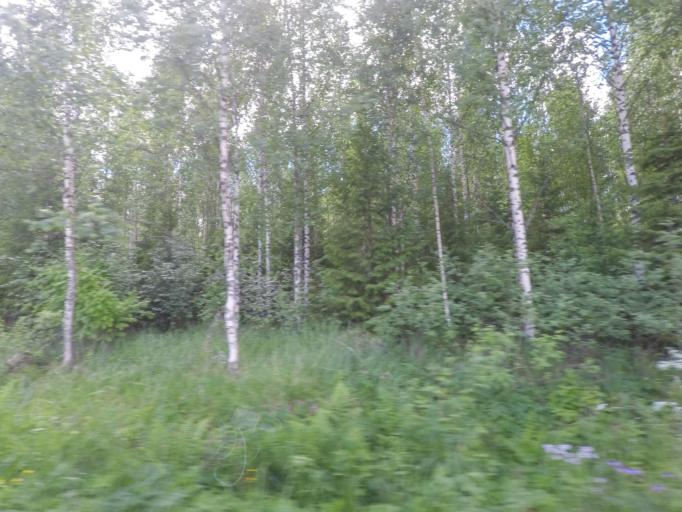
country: FI
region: Central Finland
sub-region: Jyvaeskylae
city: Hankasalmi
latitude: 62.4147
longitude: 26.6421
